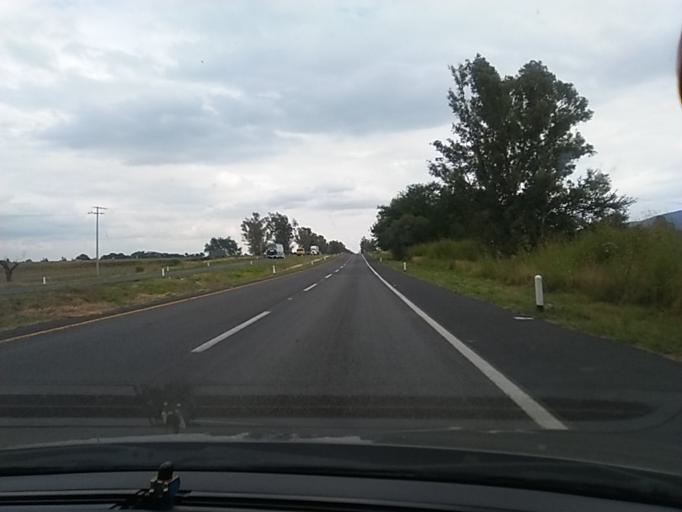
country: MX
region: Jalisco
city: Ocotlan
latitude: 20.3969
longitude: -102.7280
